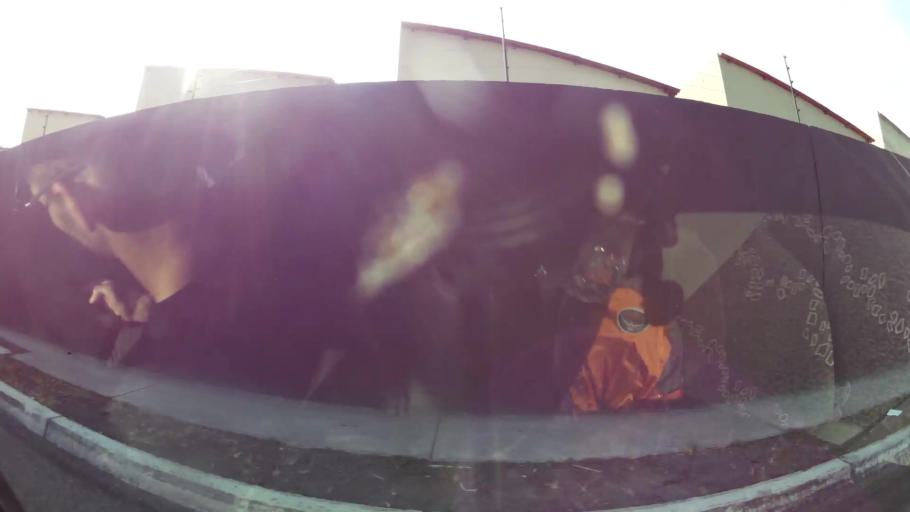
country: EC
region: Guayas
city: Santa Lucia
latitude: -2.1896
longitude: -80.0028
